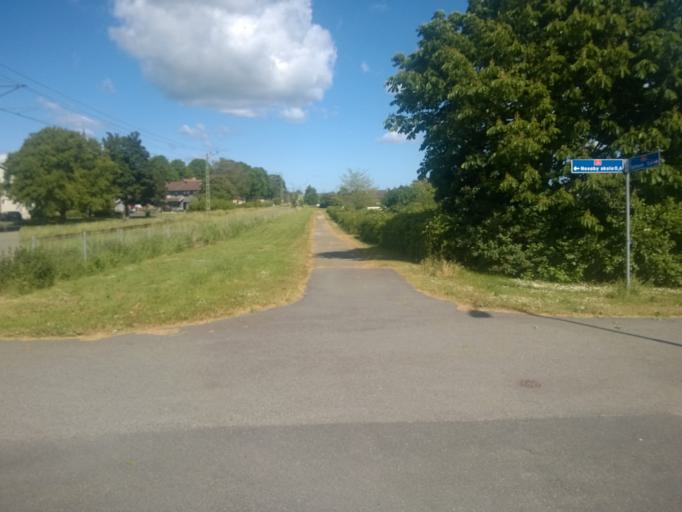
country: SE
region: Skane
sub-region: Kristianstads Kommun
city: Kristianstad
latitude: 56.0510
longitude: 14.1898
